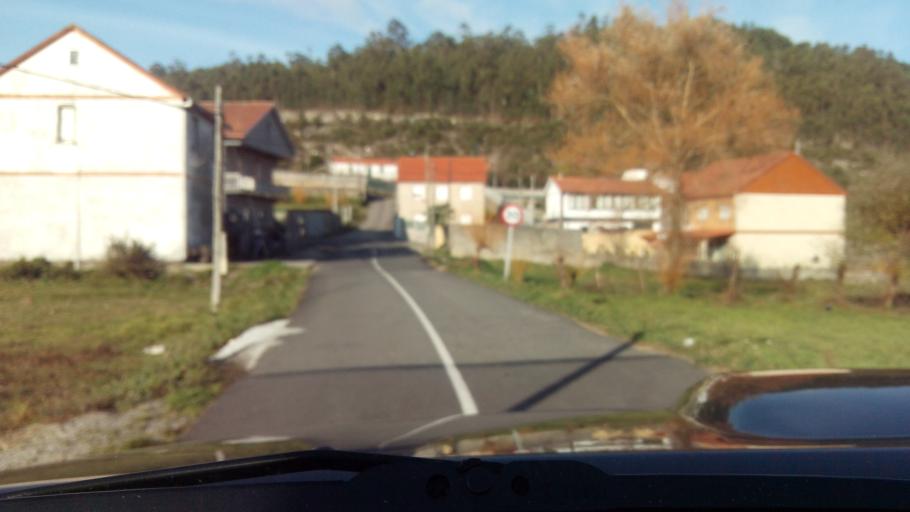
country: ES
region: Galicia
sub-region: Provincia de Pontevedra
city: Marin
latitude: 42.3656
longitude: -8.7032
